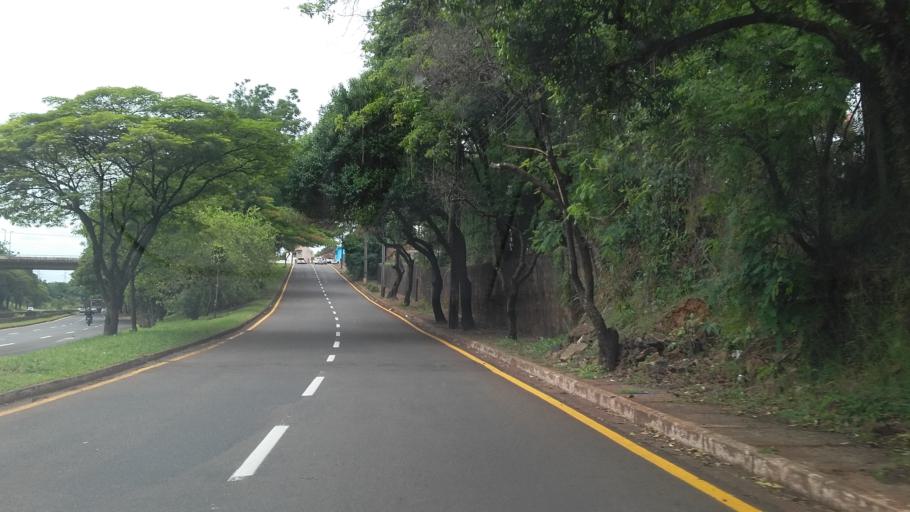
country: BR
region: Parana
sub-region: Londrina
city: Londrina
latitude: -23.3180
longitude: -51.1506
